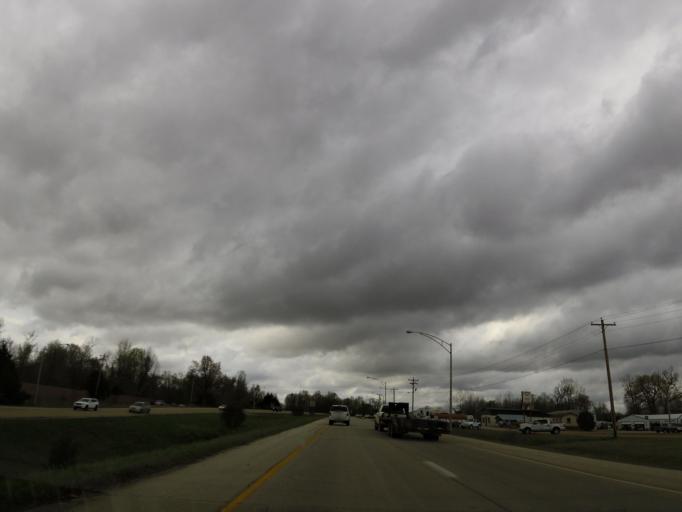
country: US
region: Missouri
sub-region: Butler County
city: Poplar Bluff
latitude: 36.7408
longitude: -90.4175
